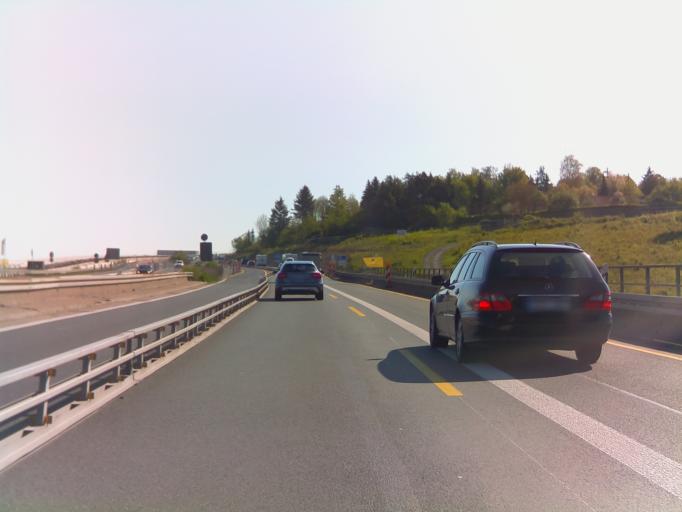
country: DE
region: Bavaria
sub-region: Regierungsbezirk Unterfranken
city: Reichenberg
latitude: 49.7520
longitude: 9.9459
